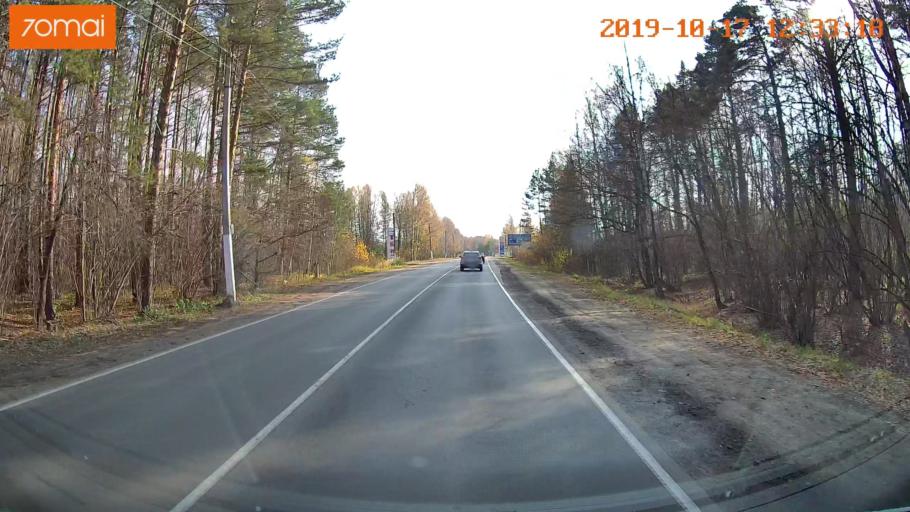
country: RU
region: Rjazan
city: Kasimov
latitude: 54.9558
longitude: 41.3526
